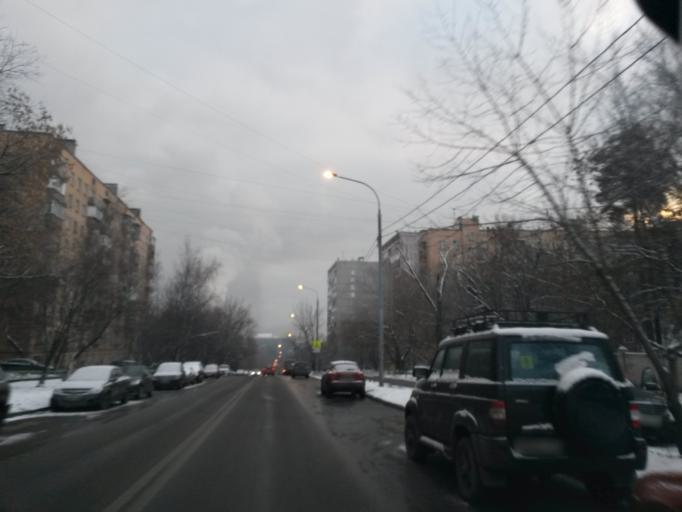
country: RU
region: Moskovskaya
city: Bol'shaya Setun'
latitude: 55.7195
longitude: 37.4371
